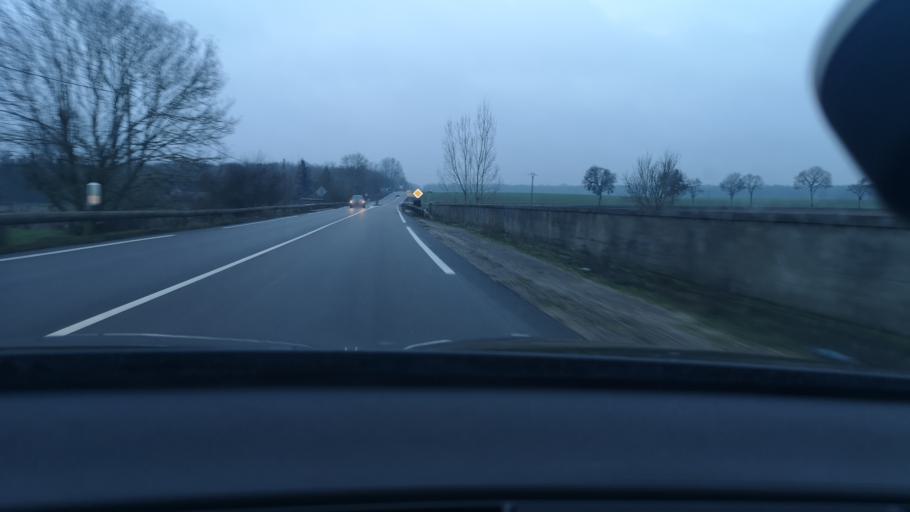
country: FR
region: Bourgogne
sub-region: Departement de la Cote-d'Or
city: Aiserey
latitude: 47.1255
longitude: 5.0984
